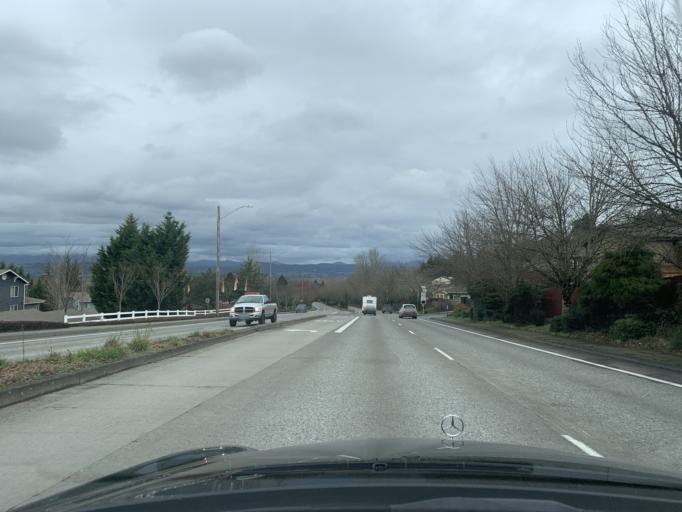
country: US
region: Oregon
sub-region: Multnomah County
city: Troutdale
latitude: 45.5356
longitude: -122.3973
